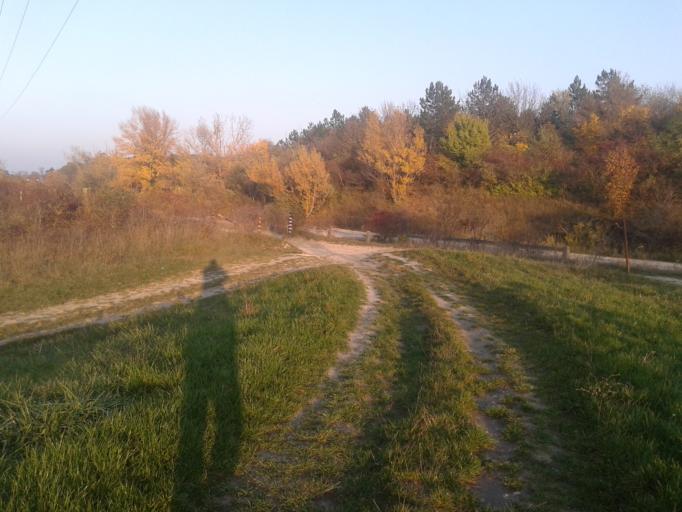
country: HU
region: Fejer
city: Fehervarcsurgo
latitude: 47.2834
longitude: 18.2584
